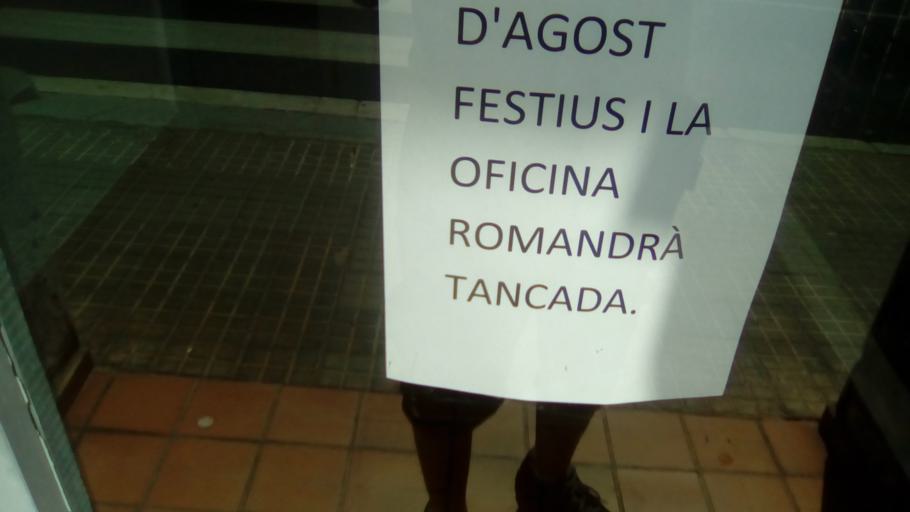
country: ES
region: Catalonia
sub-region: Provincia de Barcelona
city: Monistrol de Montserrat
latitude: 41.6292
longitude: 1.8593
